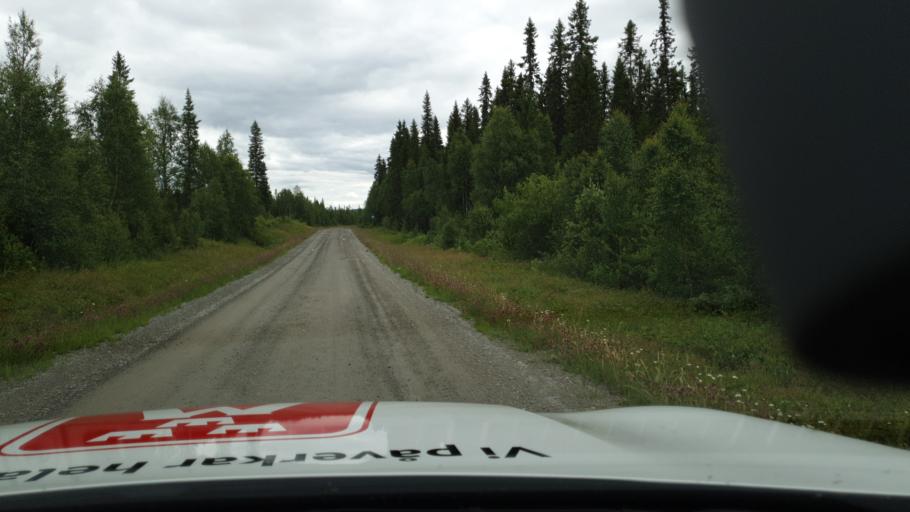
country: SE
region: Vaesterbotten
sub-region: Storumans Kommun
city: Storuman
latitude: 64.7561
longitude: 17.0783
